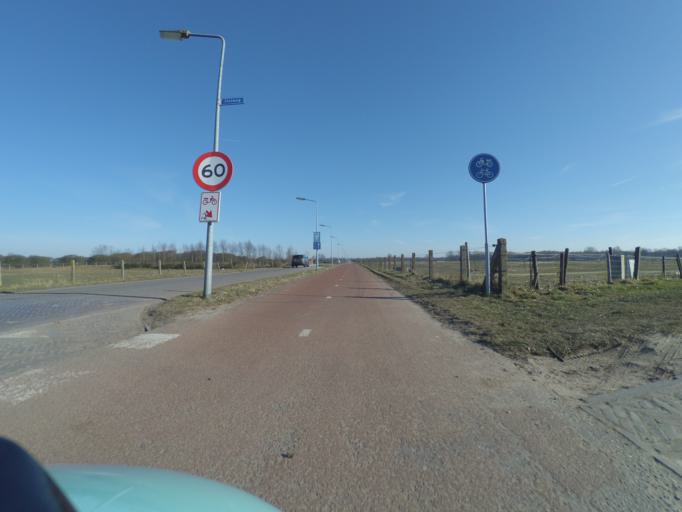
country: NL
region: North Holland
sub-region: Gemeente Blaricum
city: Blaricum
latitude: 52.2766
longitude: 5.2546
